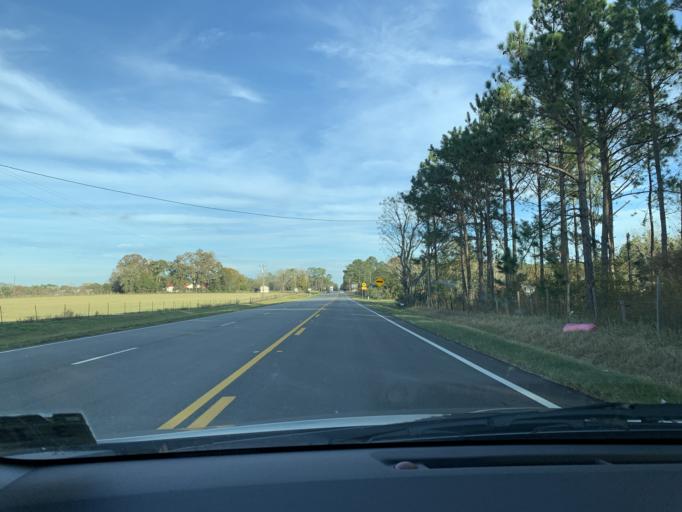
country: US
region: Georgia
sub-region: Irwin County
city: Ocilla
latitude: 31.5958
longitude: -83.1547
